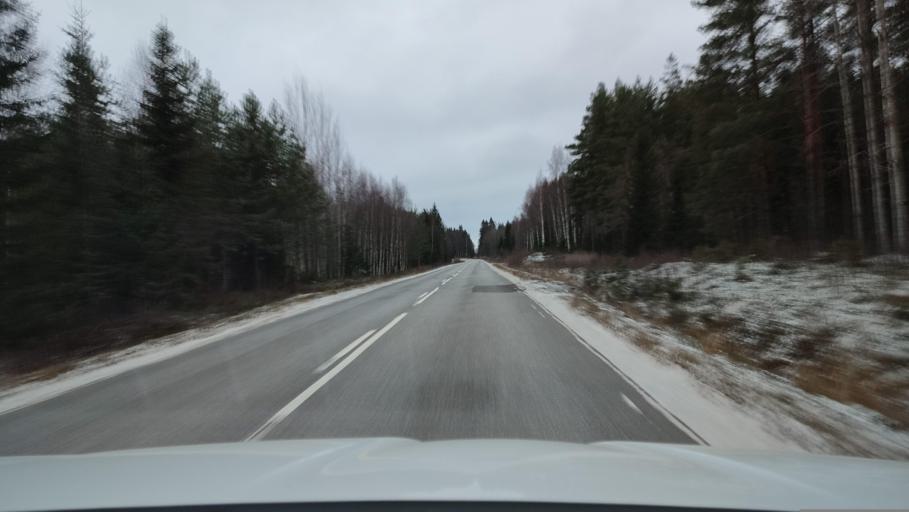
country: FI
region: Ostrobothnia
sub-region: Vaasa
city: Replot
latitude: 63.2620
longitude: 21.3610
